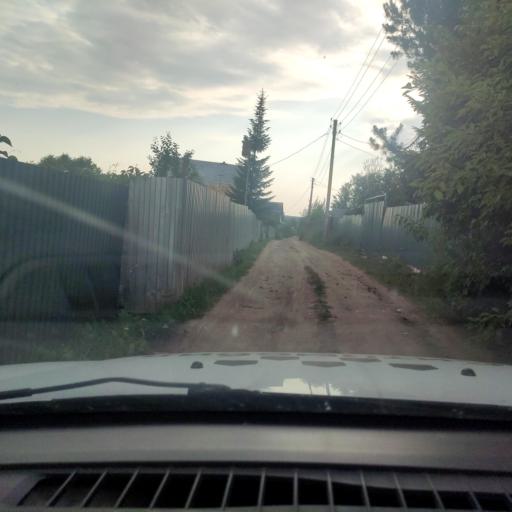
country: RU
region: Perm
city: Polazna
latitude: 58.1677
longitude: 56.3525
